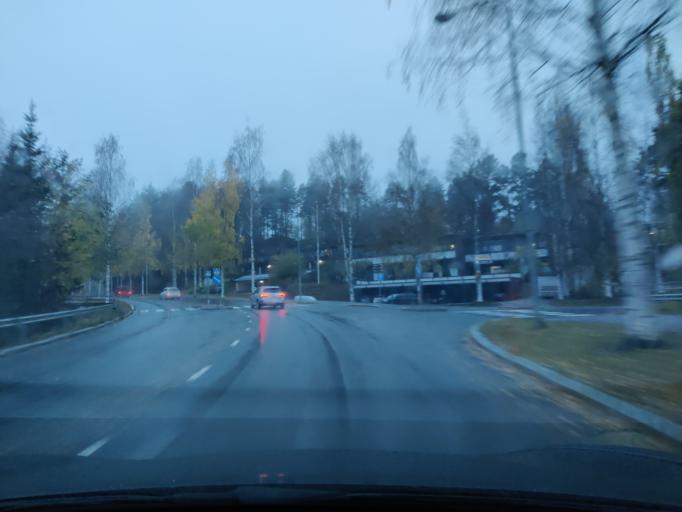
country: FI
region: Northern Savo
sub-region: Kuopio
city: Kuopio
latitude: 62.8475
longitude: 27.6473
